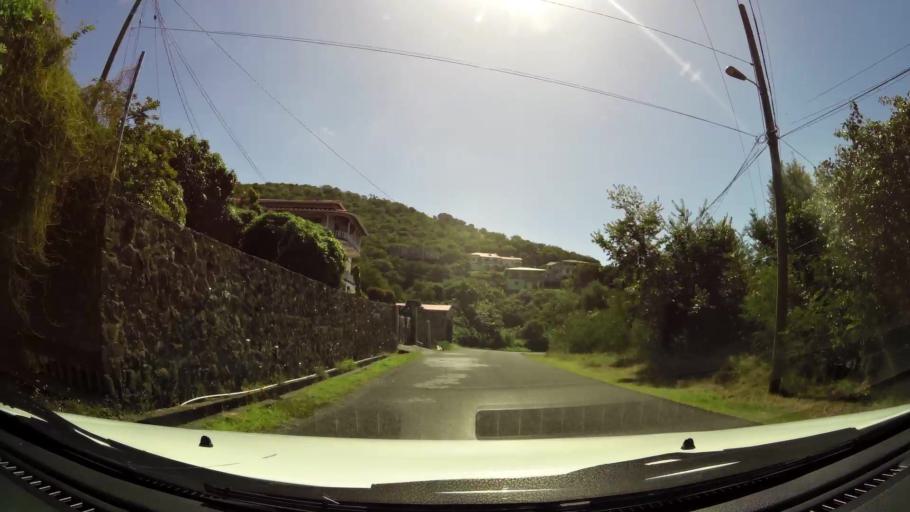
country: LC
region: Vieux-Fort
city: Vieux Fort
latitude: 13.7213
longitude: -60.9500
